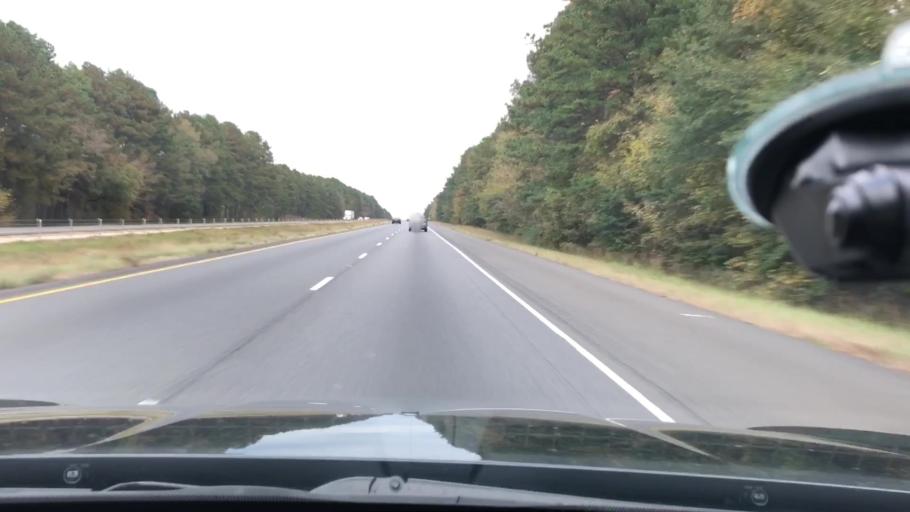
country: US
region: Arkansas
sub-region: Clark County
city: Arkadelphia
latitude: 34.2672
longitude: -92.9746
